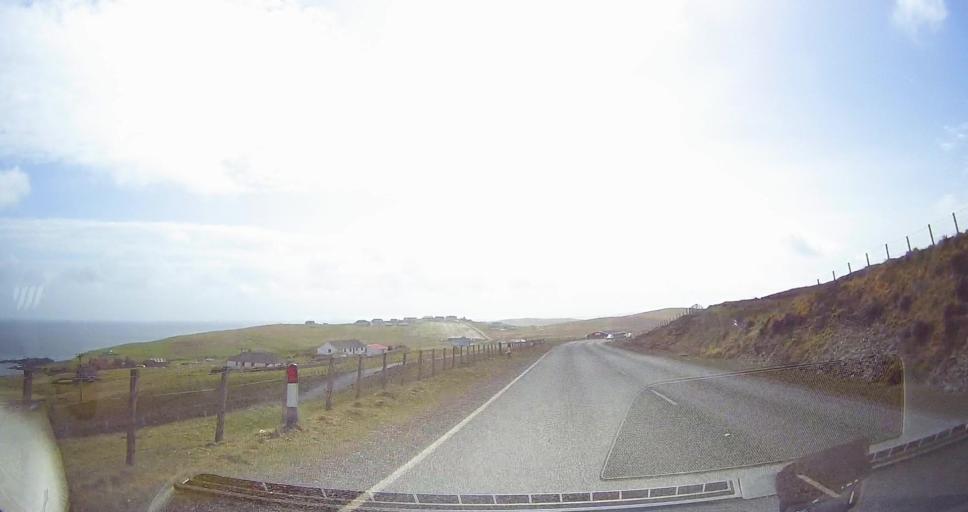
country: GB
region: Scotland
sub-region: Shetland Islands
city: Sandwick
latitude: 60.0661
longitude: -1.2237
